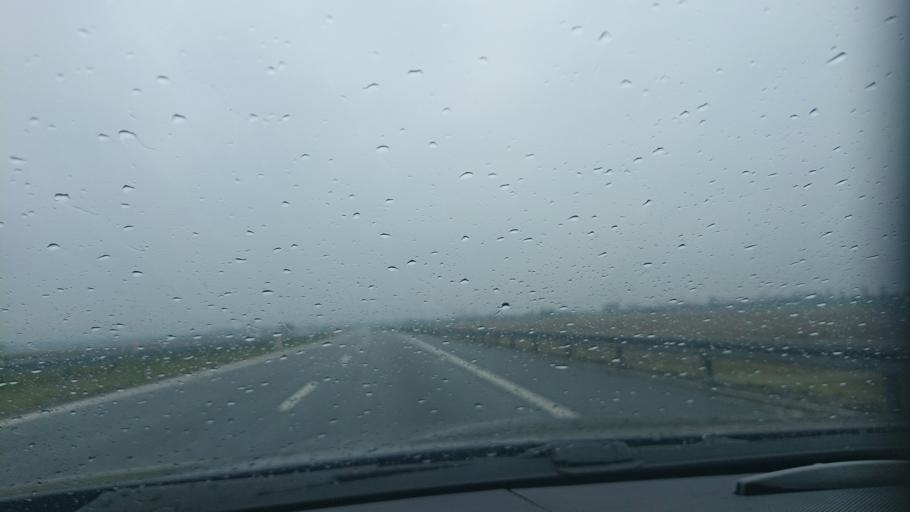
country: PL
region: Greater Poland Voivodeship
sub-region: Powiat gnieznienski
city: Gniezno
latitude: 52.5741
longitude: 17.5960
